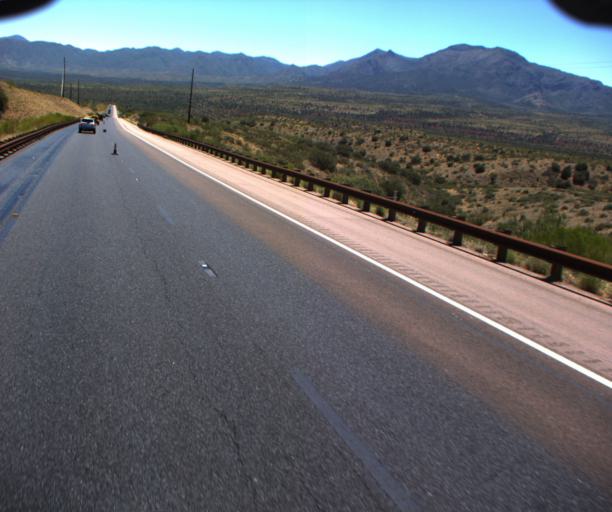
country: US
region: Arizona
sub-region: Gila County
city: Payson
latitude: 34.1386
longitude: -111.3520
